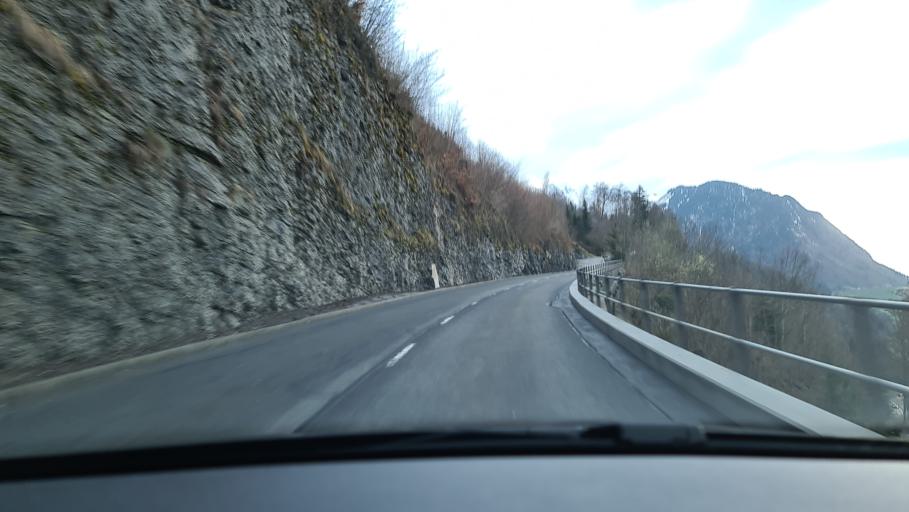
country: CH
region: Nidwalden
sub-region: Nidwalden
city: Emmetten
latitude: 46.9591
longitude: 8.5043
